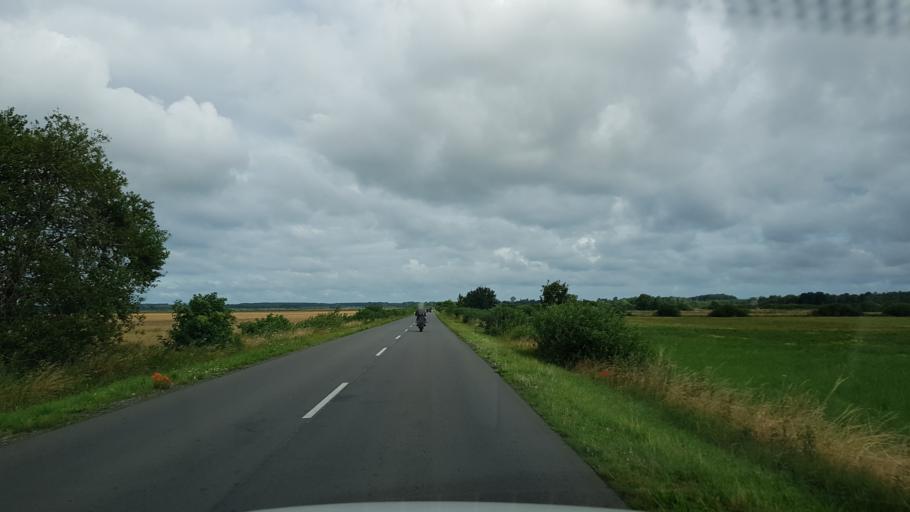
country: PL
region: West Pomeranian Voivodeship
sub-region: Powiat gryficki
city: Karnice
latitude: 54.0411
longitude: 15.0378
